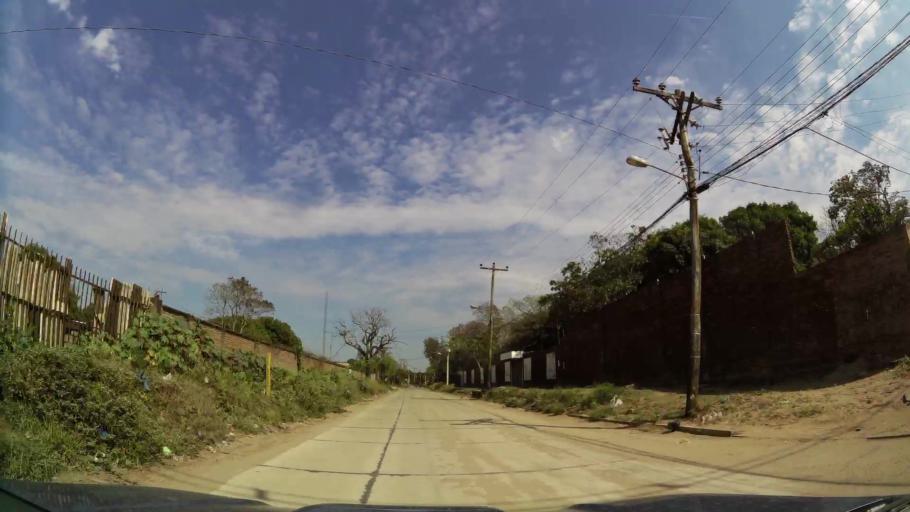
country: BO
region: Santa Cruz
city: Santa Cruz de la Sierra
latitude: -17.7200
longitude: -63.1538
